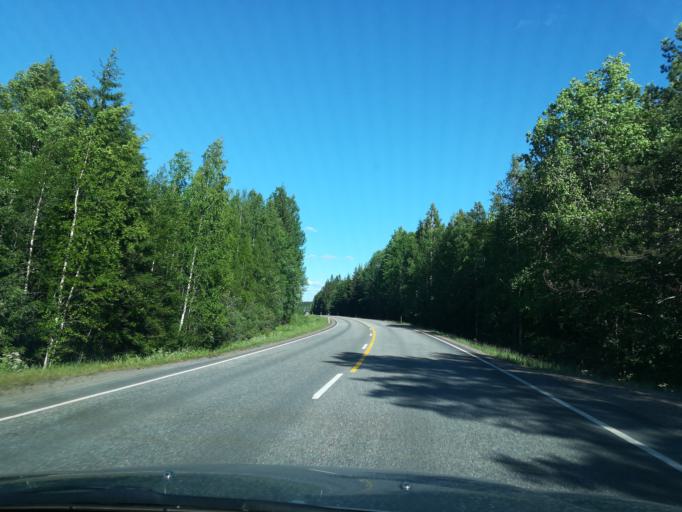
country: FI
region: South Karelia
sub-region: Imatra
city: Ruokolahti
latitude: 61.3514
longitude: 28.7361
